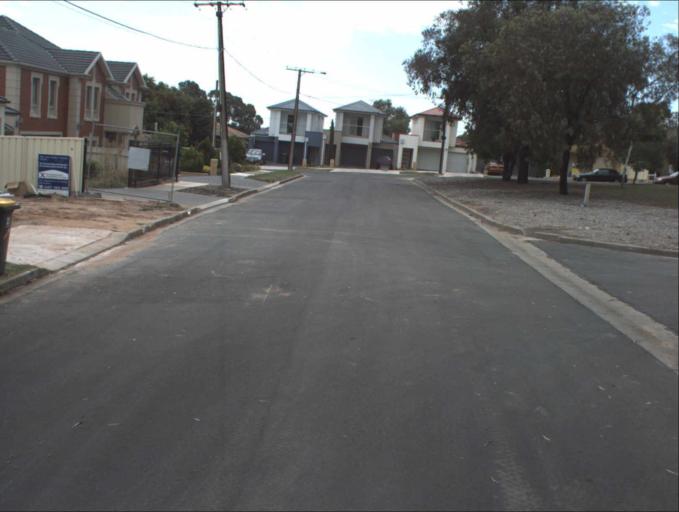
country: AU
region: South Australia
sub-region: Port Adelaide Enfield
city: Enfield
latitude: -34.8553
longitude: 138.6071
